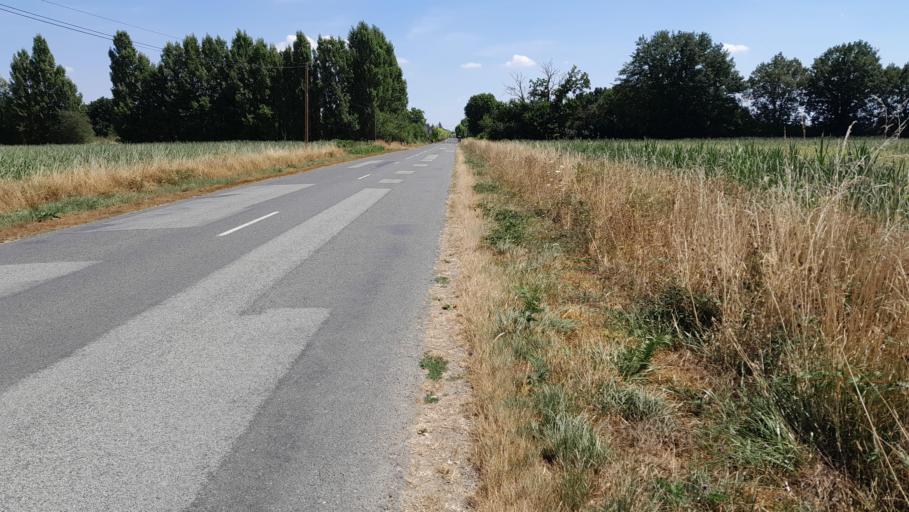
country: FR
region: Brittany
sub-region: Departement d'Ille-et-Vilaine
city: Le Pertre
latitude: 47.9665
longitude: -1.0585
